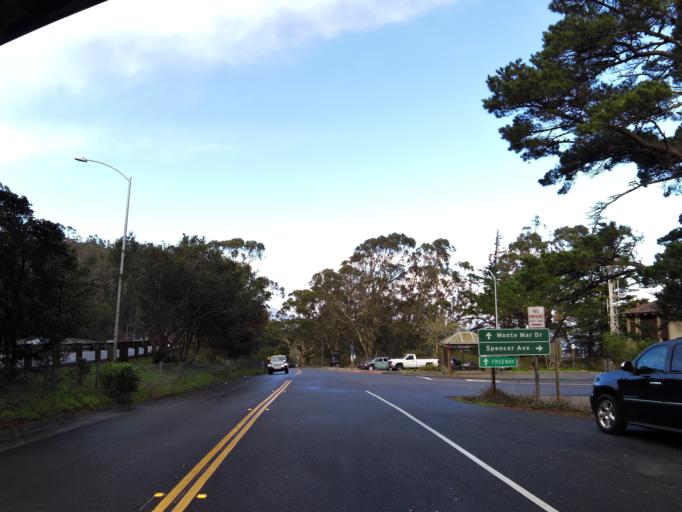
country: US
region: California
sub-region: Marin County
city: Sausalito
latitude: 37.8513
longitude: -122.4901
